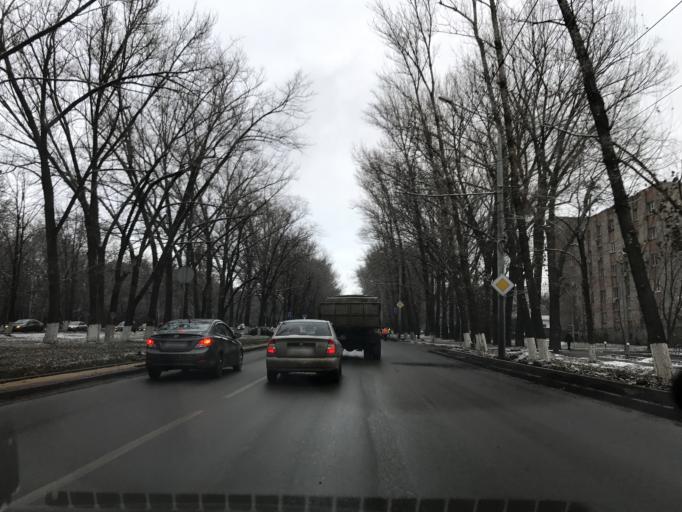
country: RU
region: Rostov
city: Aksay
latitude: 47.2634
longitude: 39.8114
